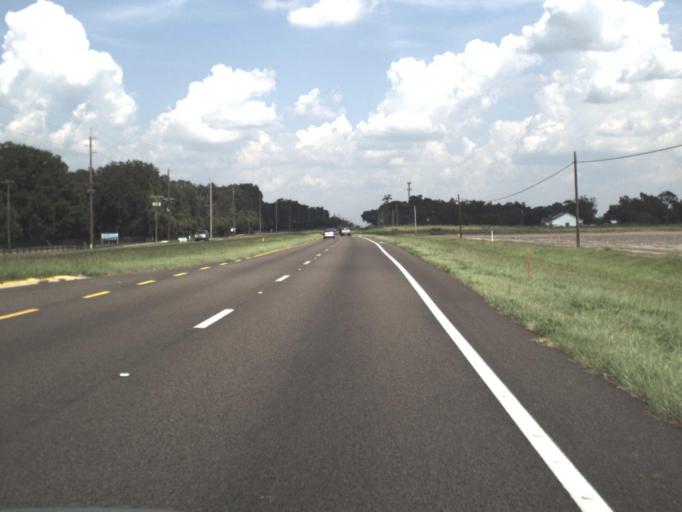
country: US
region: Florida
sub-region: Hillsborough County
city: Plant City
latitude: 27.9375
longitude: -82.1441
